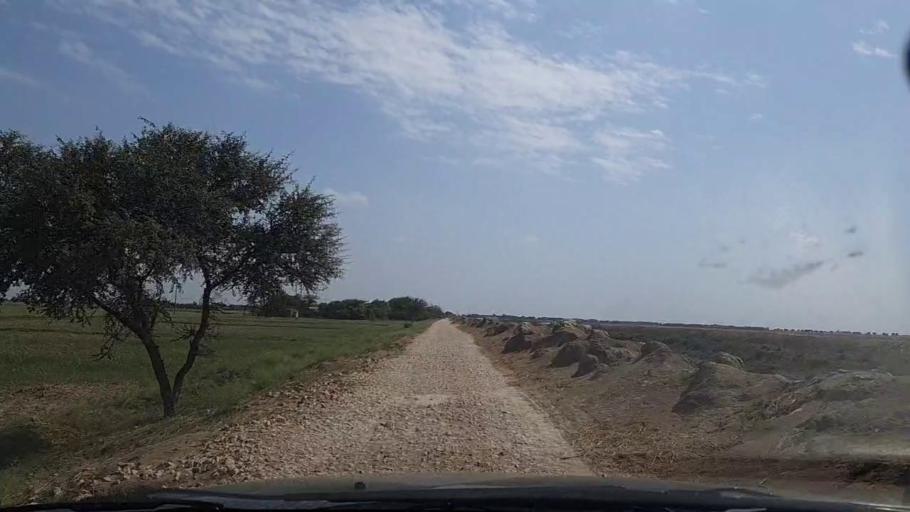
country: PK
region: Sindh
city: Mirpur Batoro
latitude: 24.5763
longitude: 68.1963
